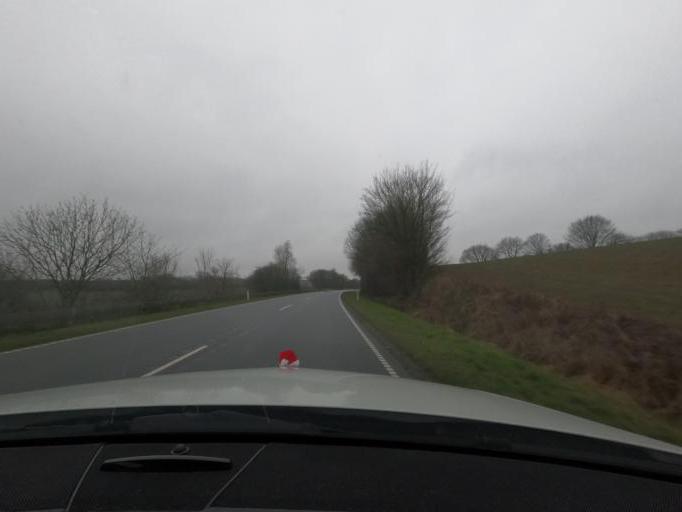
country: DK
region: South Denmark
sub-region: Haderslev Kommune
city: Haderslev
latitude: 55.1882
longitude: 9.4107
